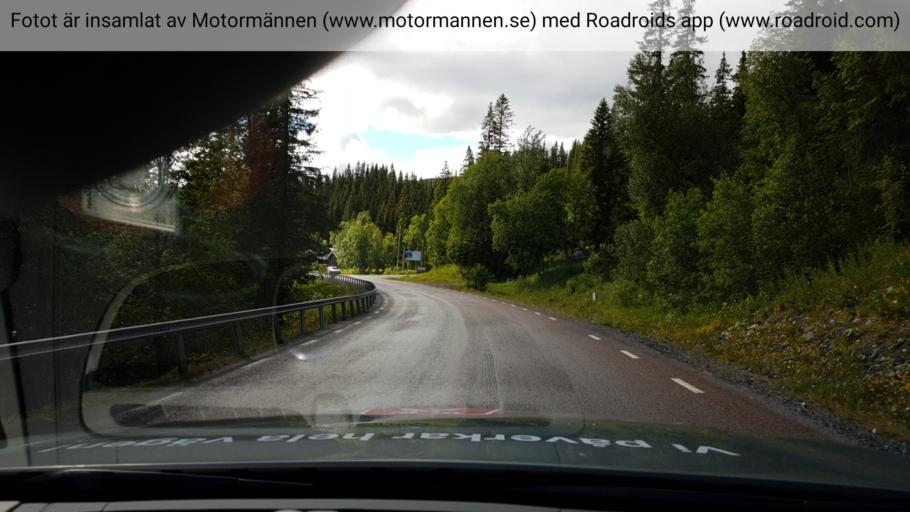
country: SE
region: Jaemtland
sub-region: Are Kommun
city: Jarpen
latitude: 63.1056
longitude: 13.8241
